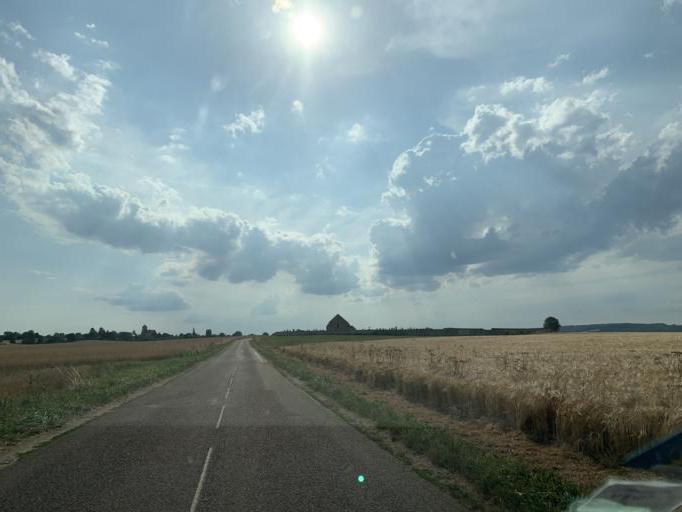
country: FR
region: Bourgogne
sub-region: Departement de l'Yonne
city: Fontenailles
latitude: 47.5069
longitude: 3.3615
